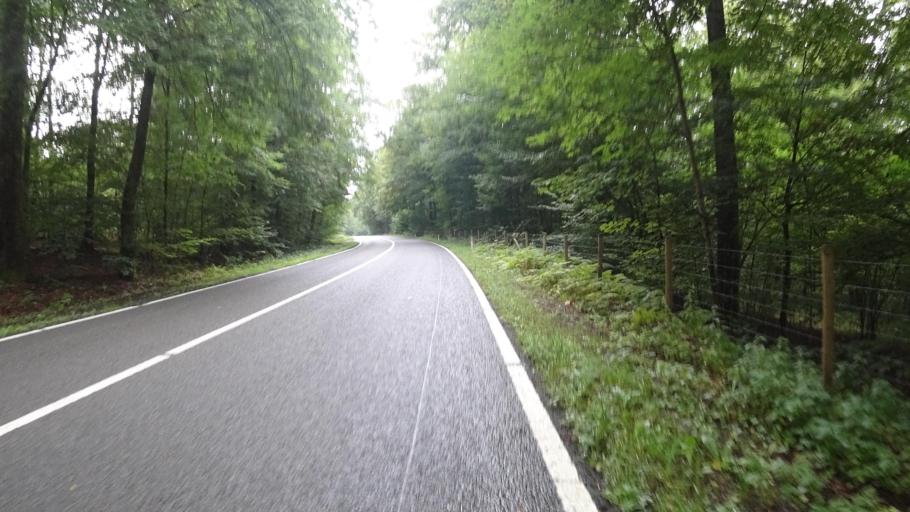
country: BE
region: Wallonia
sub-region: Province du Luxembourg
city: Chiny
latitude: 49.7842
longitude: 5.3364
